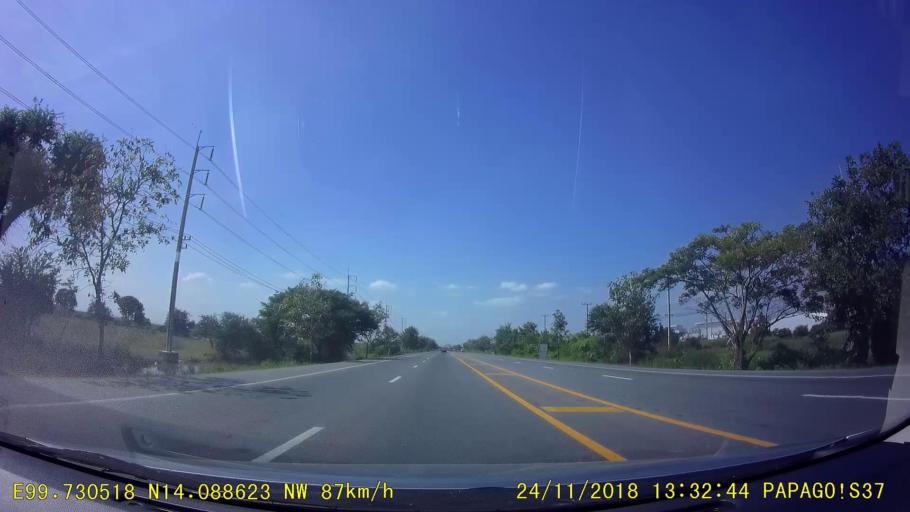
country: TH
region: Kanchanaburi
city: Phanom Thuan
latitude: 14.0875
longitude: 99.7325
